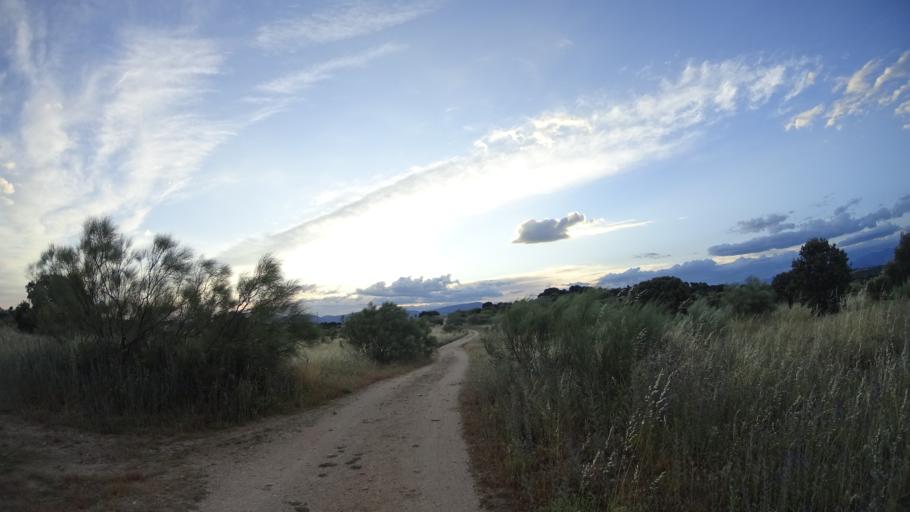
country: ES
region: Madrid
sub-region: Provincia de Madrid
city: Colmenarejo
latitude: 40.5322
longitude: -4.0005
